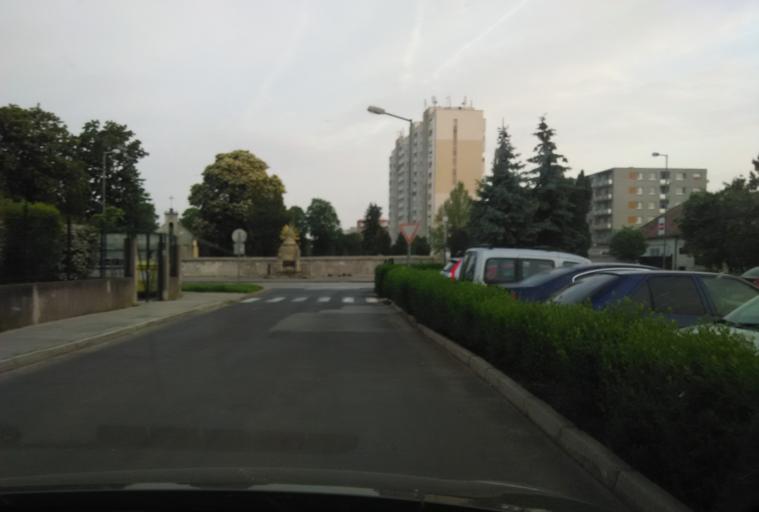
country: SK
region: Trnavsky
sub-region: Okres Trnava
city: Trnava
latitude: 48.3813
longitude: 17.5773
